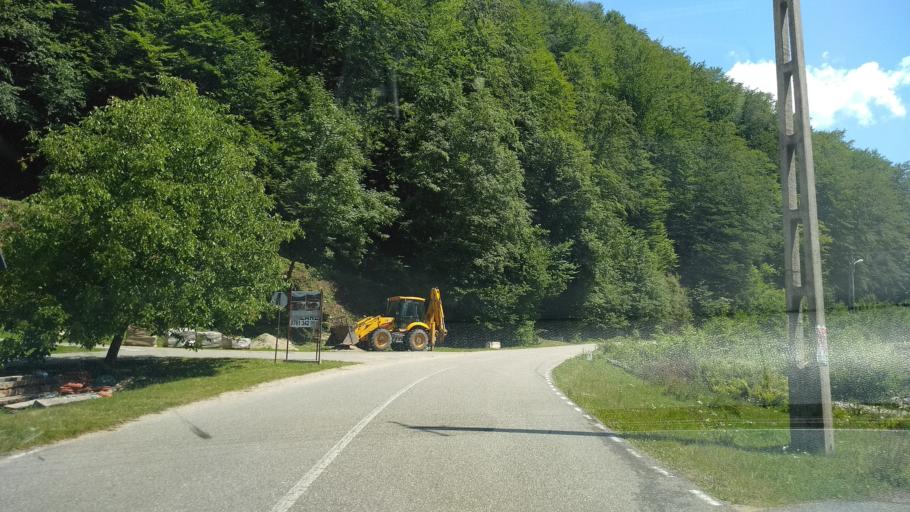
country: RO
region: Hunedoara
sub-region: Comuna Orastioara de Sus
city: Orastioara de Sus
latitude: 45.6321
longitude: 23.2155
